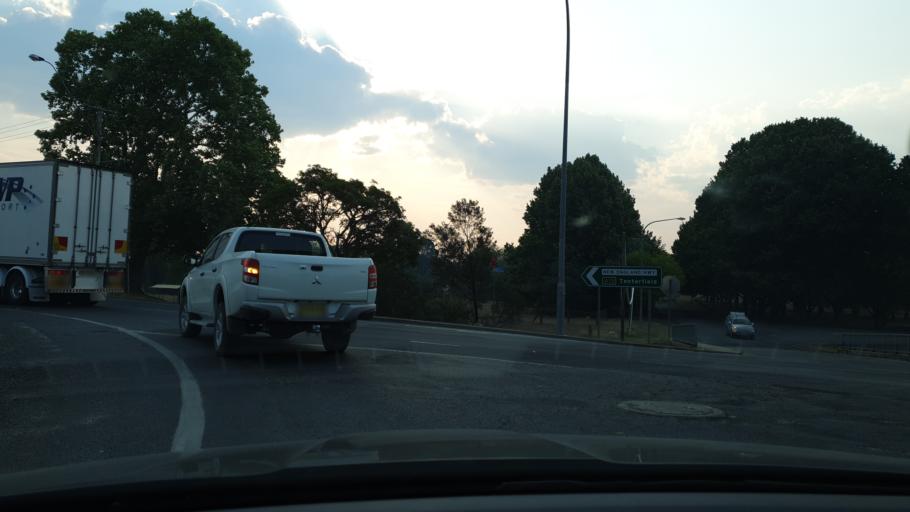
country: AU
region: New South Wales
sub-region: Tenterfield Municipality
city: Carrolls Creek
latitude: -29.0457
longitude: 152.0209
